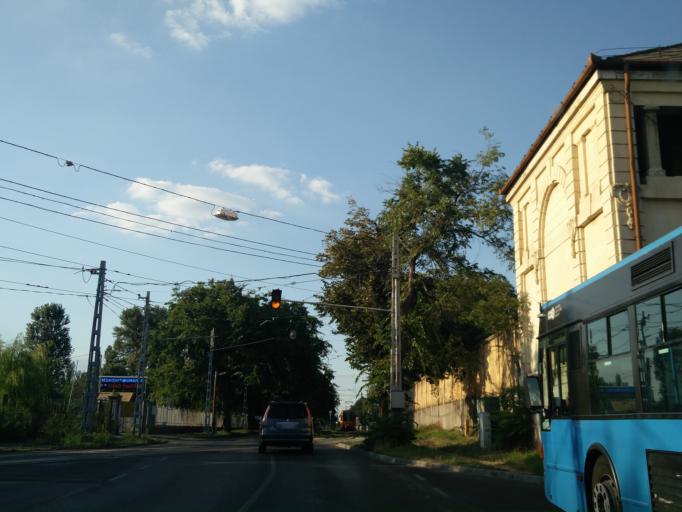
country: HU
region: Budapest
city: Budapest X. keruelet
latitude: 47.4735
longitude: 19.1782
